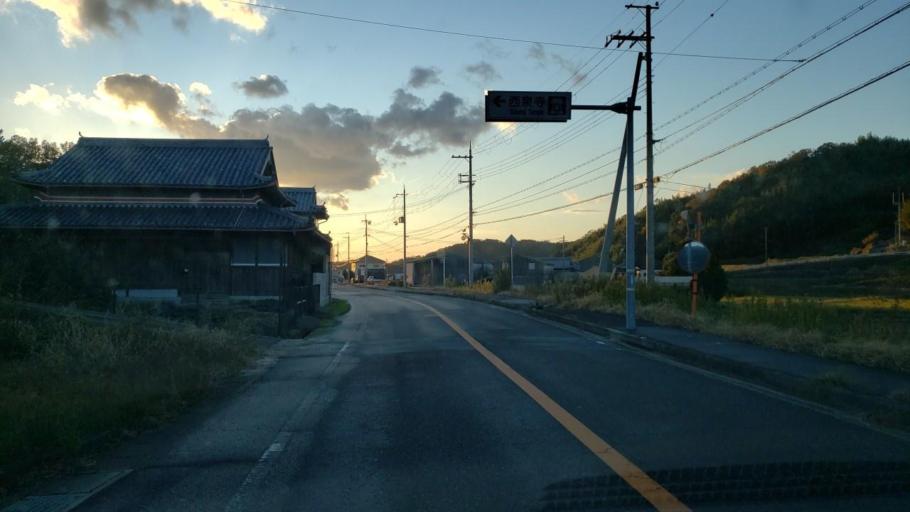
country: JP
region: Hyogo
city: Sumoto
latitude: 34.4007
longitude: 134.8254
